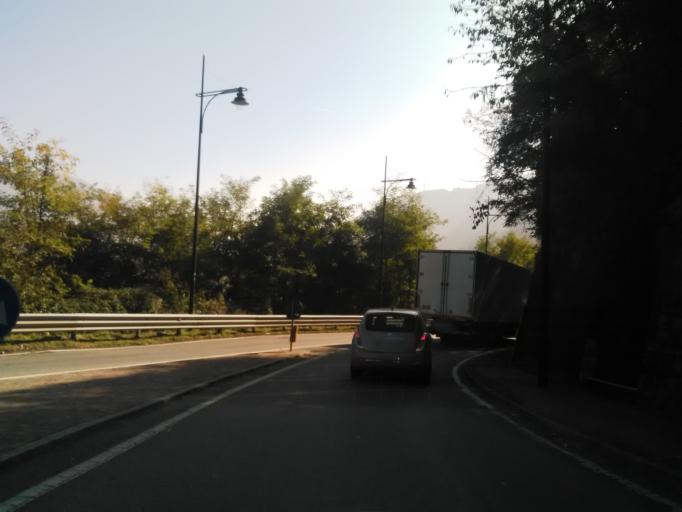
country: IT
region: Piedmont
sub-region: Provincia di Vercelli
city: Borgosesia
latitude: 45.7150
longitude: 8.2642
